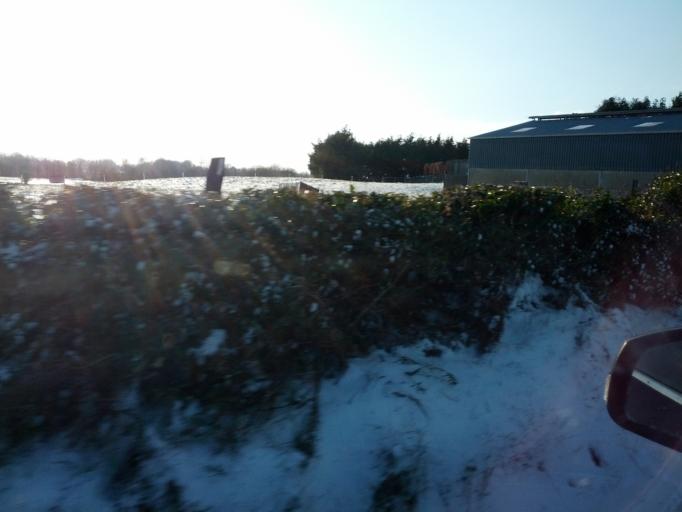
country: IE
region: Connaught
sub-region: County Galway
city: Athenry
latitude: 53.1863
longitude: -8.7235
